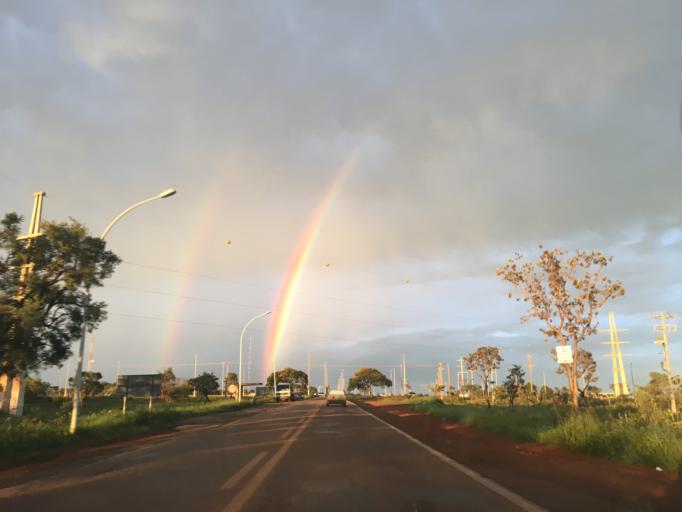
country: BR
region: Federal District
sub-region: Brasilia
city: Brasilia
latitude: -15.9764
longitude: -47.9876
